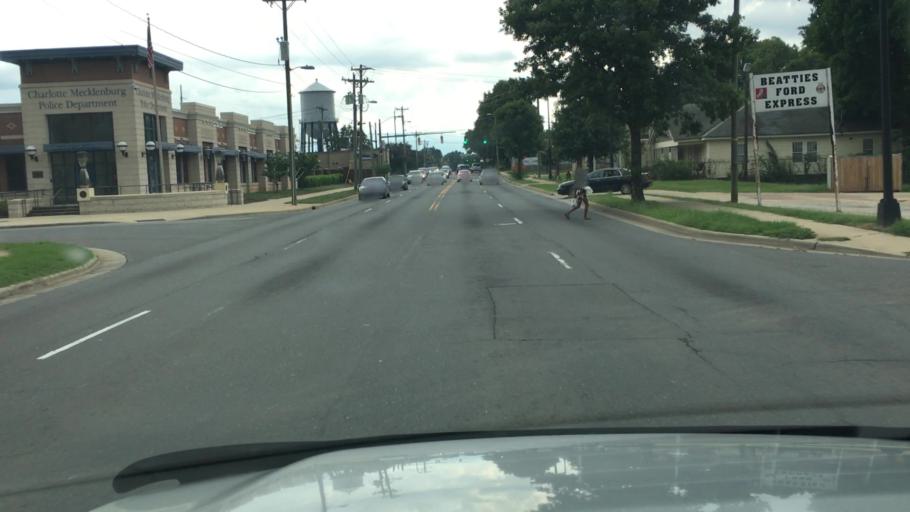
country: US
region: North Carolina
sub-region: Mecklenburg County
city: Charlotte
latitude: 35.2540
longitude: -80.8559
